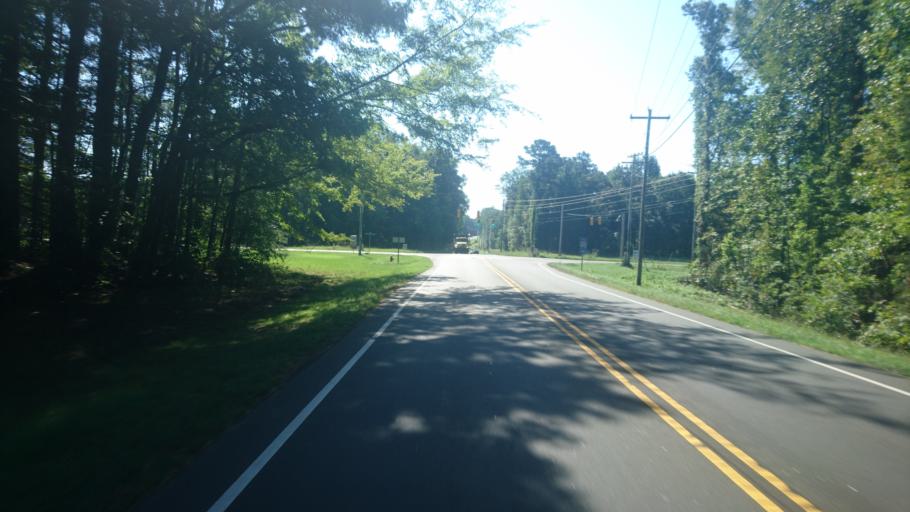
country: US
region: North Carolina
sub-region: Orange County
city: Hillsborough
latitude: 36.0178
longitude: -79.0761
